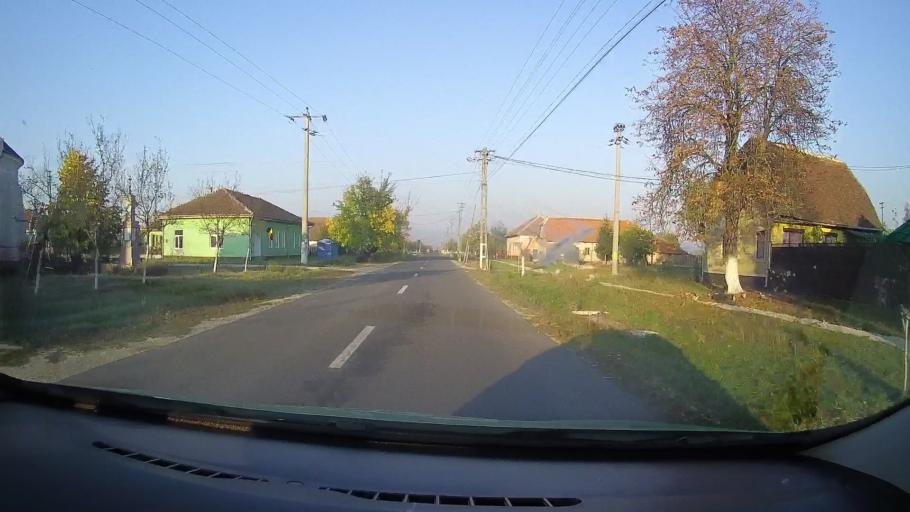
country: RO
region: Arad
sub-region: Comuna Barsa
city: Barsa
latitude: 46.3575
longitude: 22.0259
